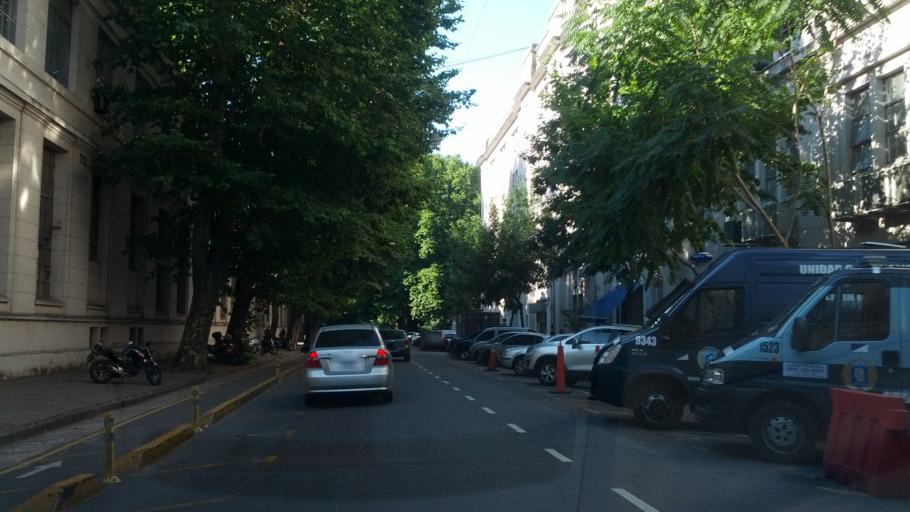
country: AR
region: Buenos Aires F.D.
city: Buenos Aires
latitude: -34.6157
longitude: -58.3676
